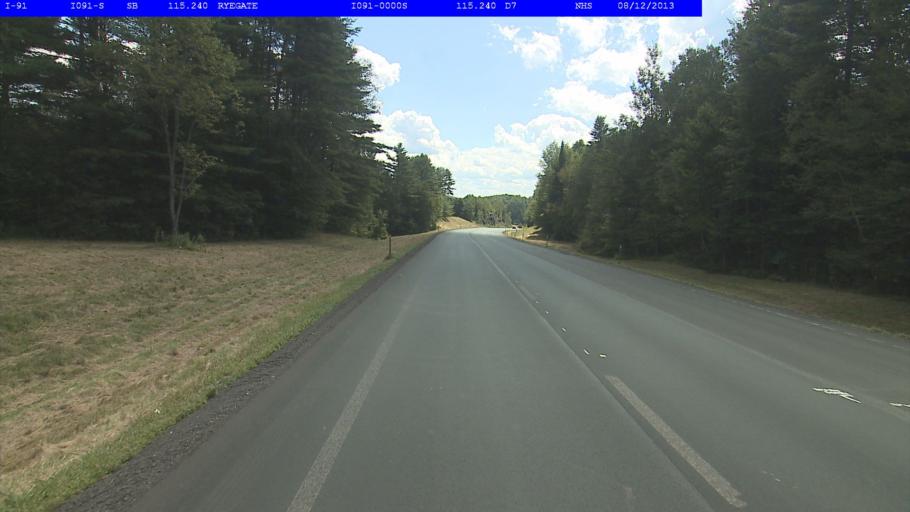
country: US
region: New Hampshire
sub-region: Grafton County
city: Woodsville
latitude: 44.2286
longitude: -72.0688
